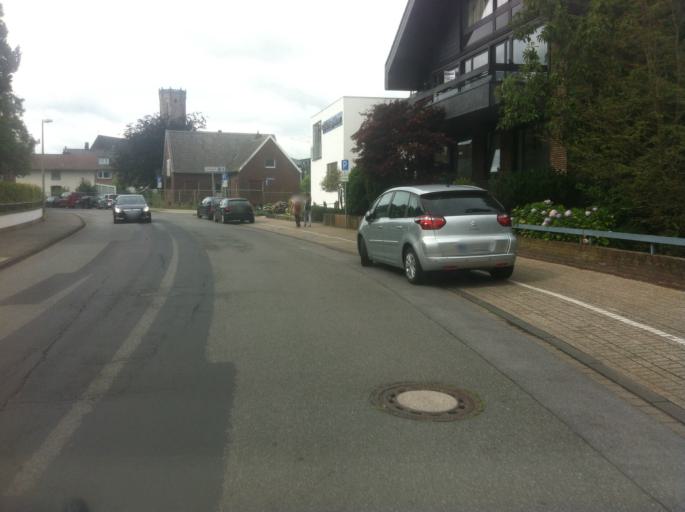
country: DE
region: North Rhine-Westphalia
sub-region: Regierungsbezirk Dusseldorf
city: Emmerich
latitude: 51.8321
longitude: 6.2478
